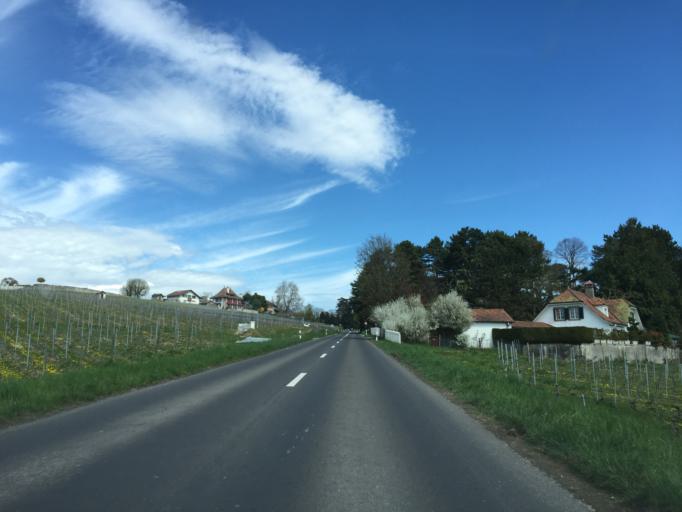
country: CH
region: Vaud
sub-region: Morges District
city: Morges
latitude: 46.5195
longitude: 6.4893
